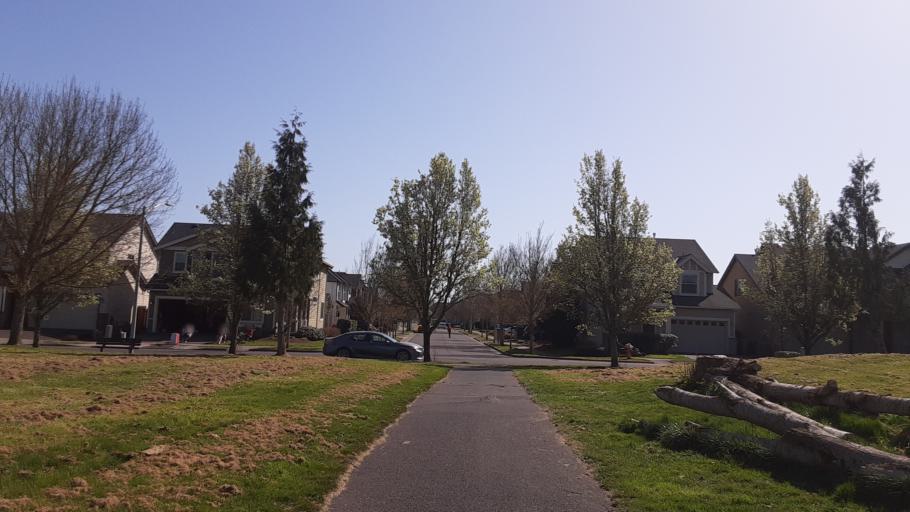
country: US
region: Oregon
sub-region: Benton County
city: Corvallis
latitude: 44.5303
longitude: -123.2609
